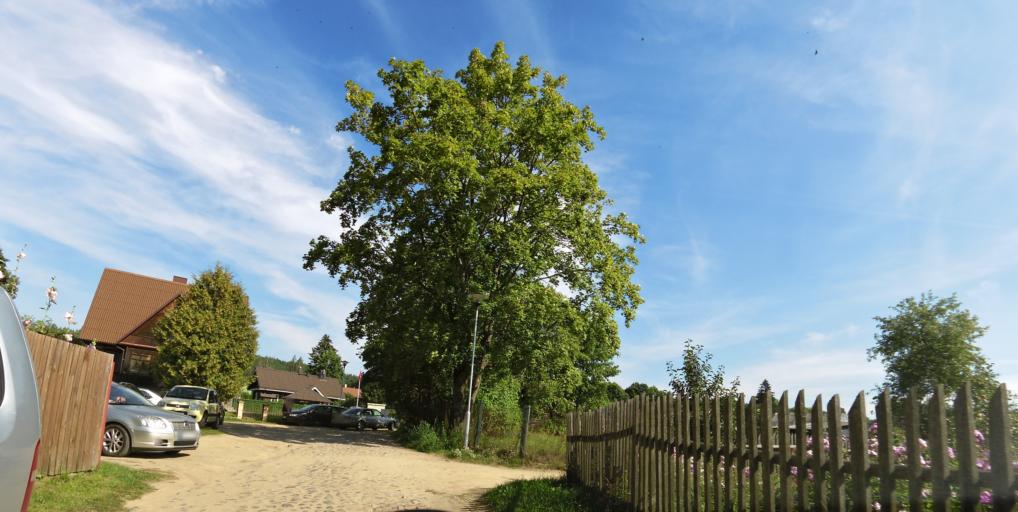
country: LT
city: Grigiskes
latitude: 54.7308
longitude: 25.0452
